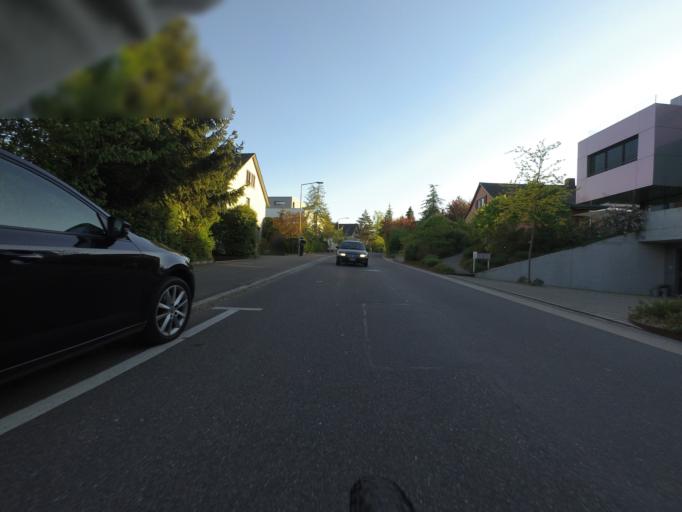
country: CH
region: Zurich
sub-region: Bezirk Winterthur
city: Oberwinterthur (Kreis 2) / Talacker
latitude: 47.5093
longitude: 8.7534
